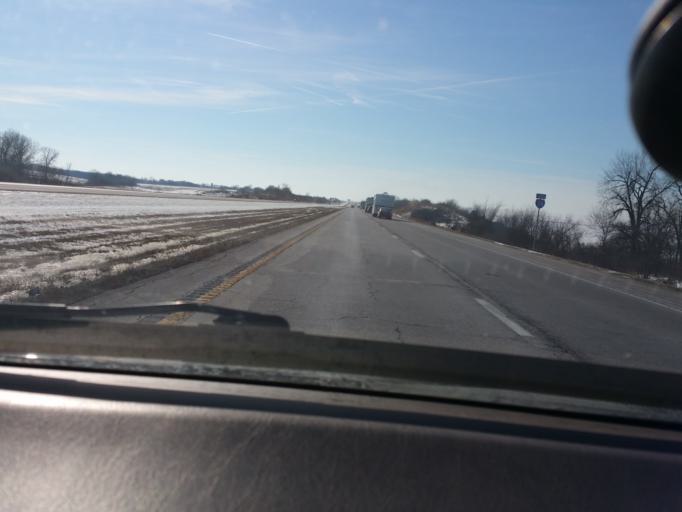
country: US
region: Missouri
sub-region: Harrison County
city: Bethany
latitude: 40.3684
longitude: -94.0048
